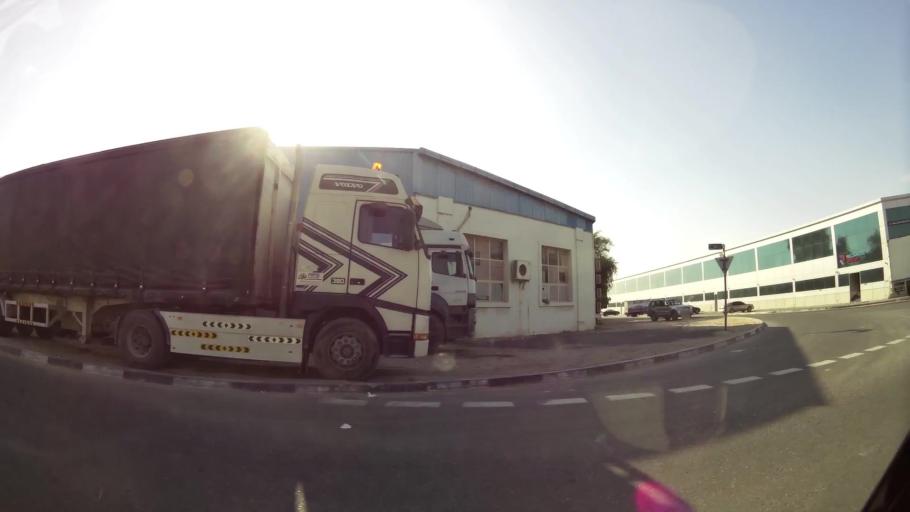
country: AE
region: Dubai
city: Dubai
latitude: 25.1189
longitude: 55.2384
